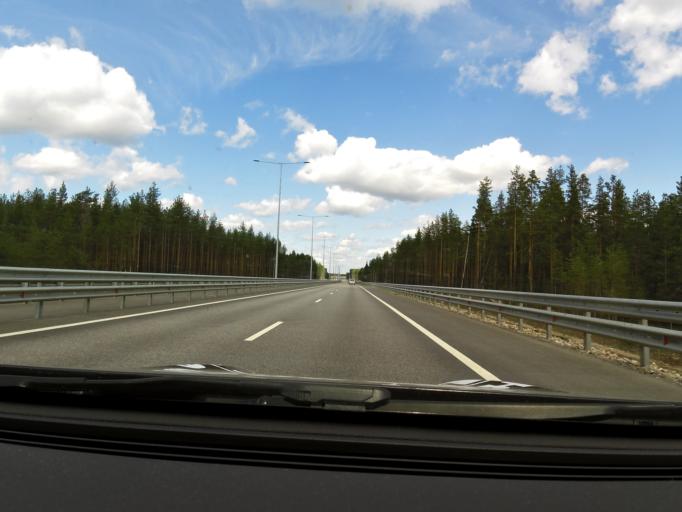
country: RU
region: Tverskaya
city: Krasnomayskiy
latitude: 57.6115
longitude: 34.2473
